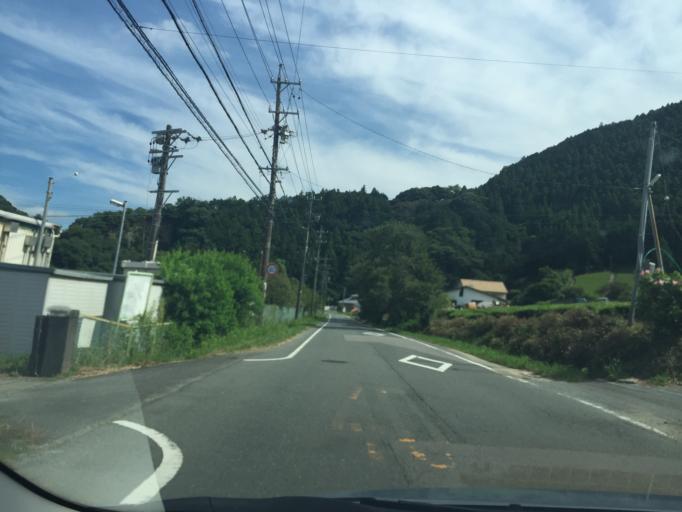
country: JP
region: Shizuoka
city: Kanaya
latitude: 34.8028
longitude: 138.0723
